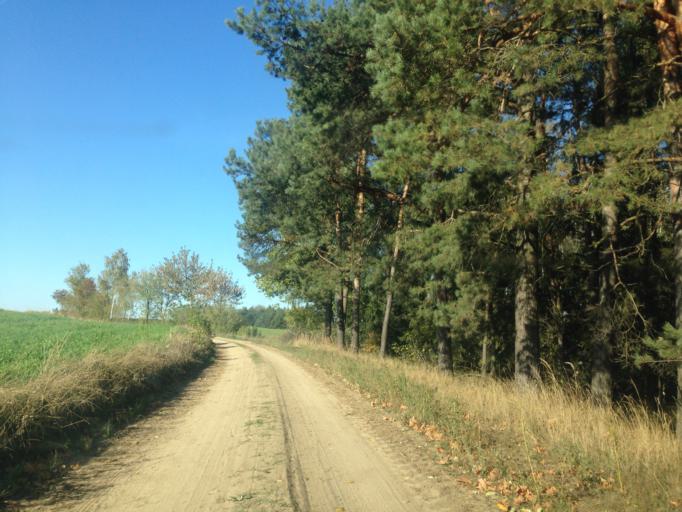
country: PL
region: Kujawsko-Pomorskie
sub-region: Powiat brodnicki
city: Bartniczka
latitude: 53.2818
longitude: 19.6773
